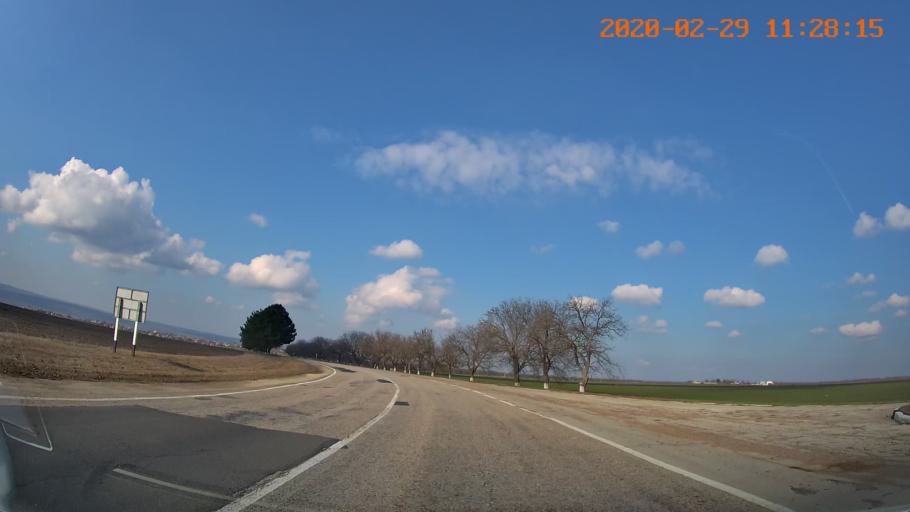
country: MD
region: Telenesti
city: Cocieri
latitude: 47.4804
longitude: 29.1388
